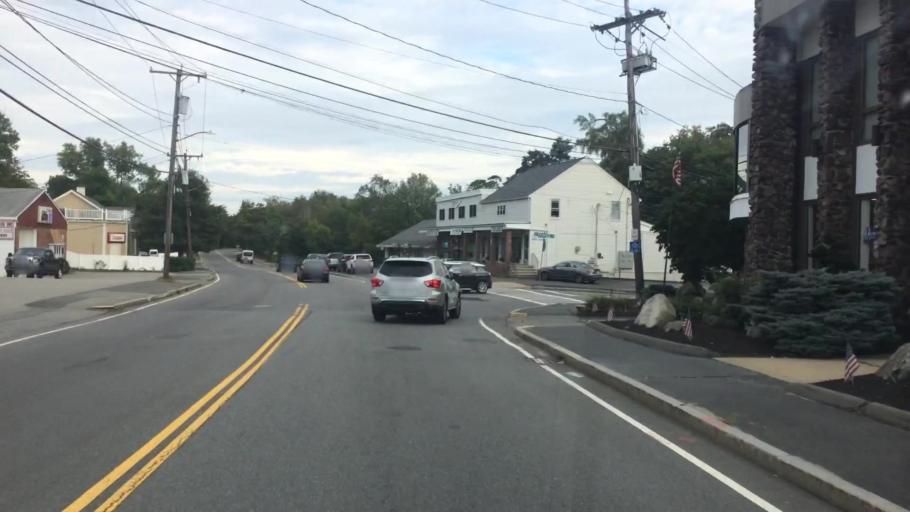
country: US
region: Massachusetts
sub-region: Middlesex County
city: Burlington
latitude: 42.4915
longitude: -71.1746
